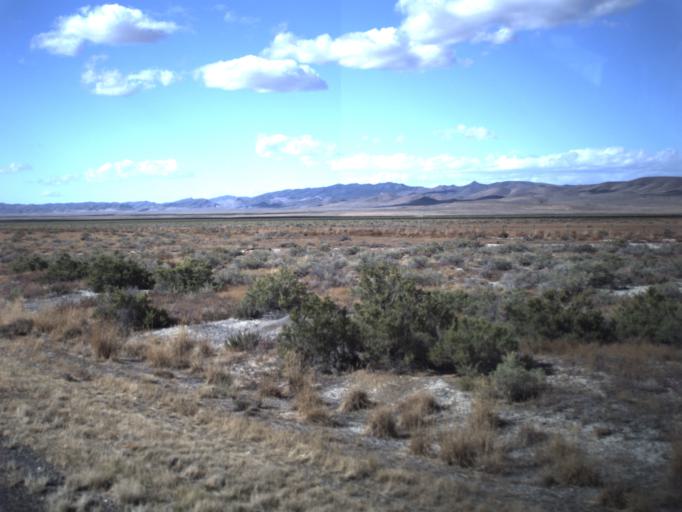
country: US
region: Utah
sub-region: Millard County
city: Delta
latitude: 39.0706
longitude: -112.7594
